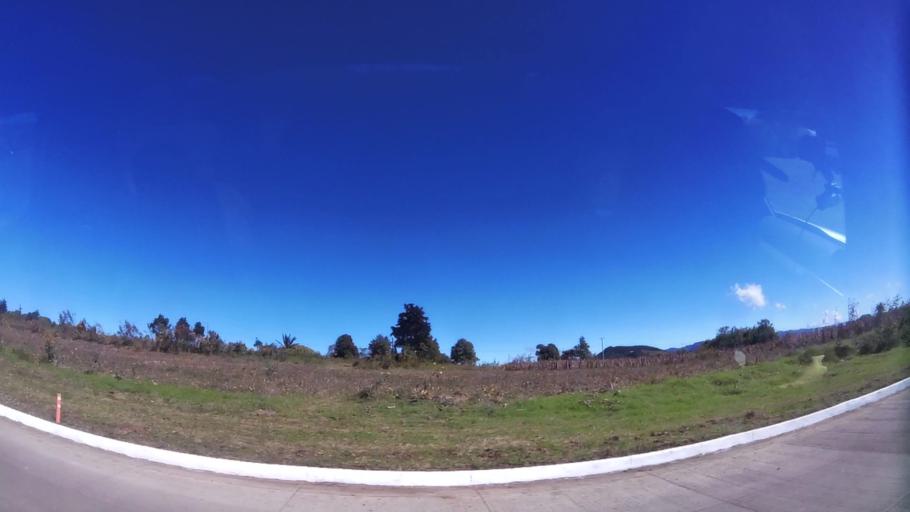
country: GT
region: Guatemala
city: San Jose Pinula
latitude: 14.5168
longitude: -90.4514
